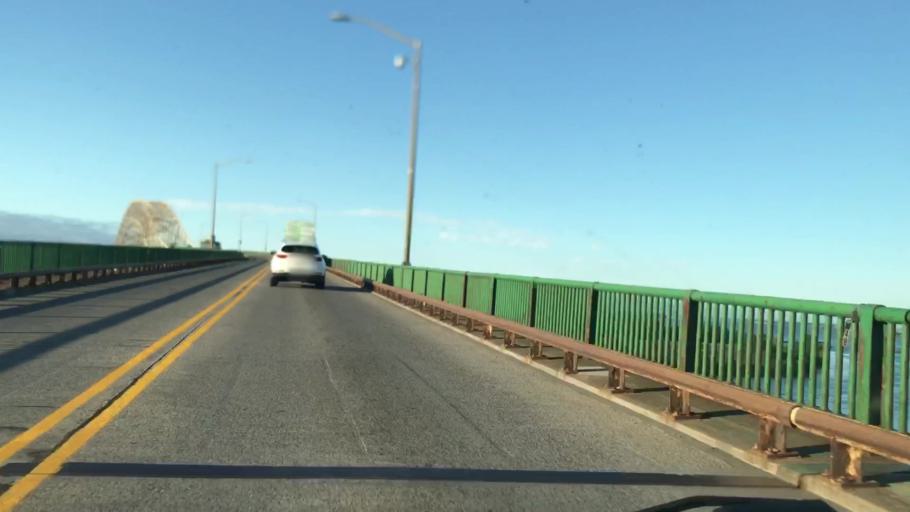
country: CA
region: Ontario
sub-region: Algoma
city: Sault Ste. Marie
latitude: 46.5167
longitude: -84.3566
